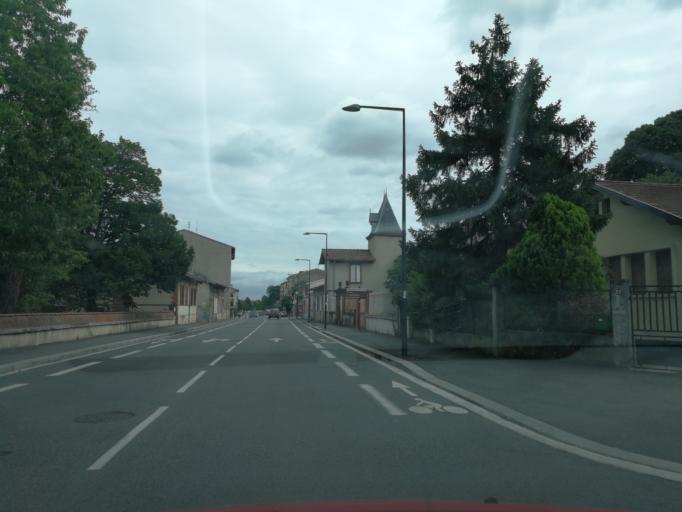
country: FR
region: Midi-Pyrenees
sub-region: Departement de la Haute-Garonne
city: Ramonville-Saint-Agne
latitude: 43.5476
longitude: 1.4727
